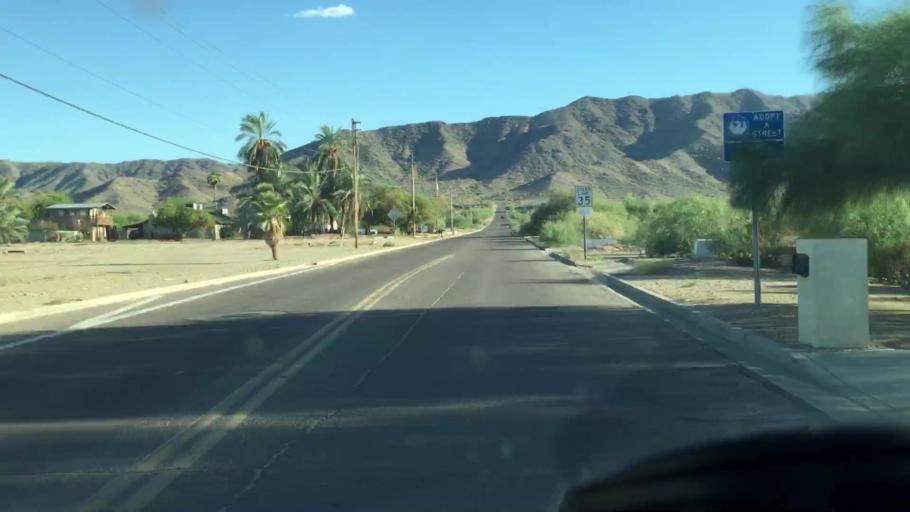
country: US
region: Arizona
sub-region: Maricopa County
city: Laveen
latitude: 33.3661
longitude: -112.0990
